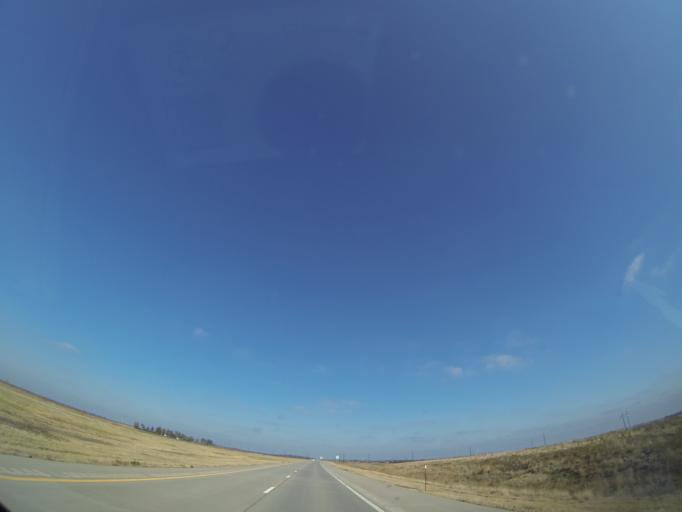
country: US
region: Kansas
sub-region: McPherson County
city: Inman
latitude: 38.1887
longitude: -97.8117
